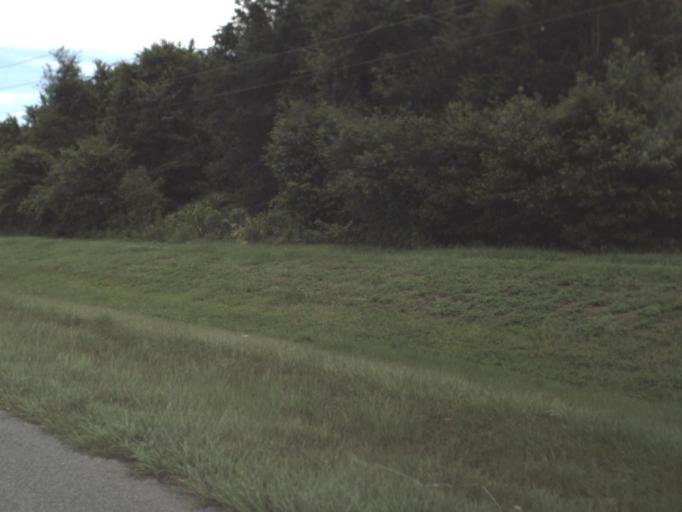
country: US
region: Florida
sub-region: Pasco County
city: Land O' Lakes
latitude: 28.1885
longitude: -82.3998
